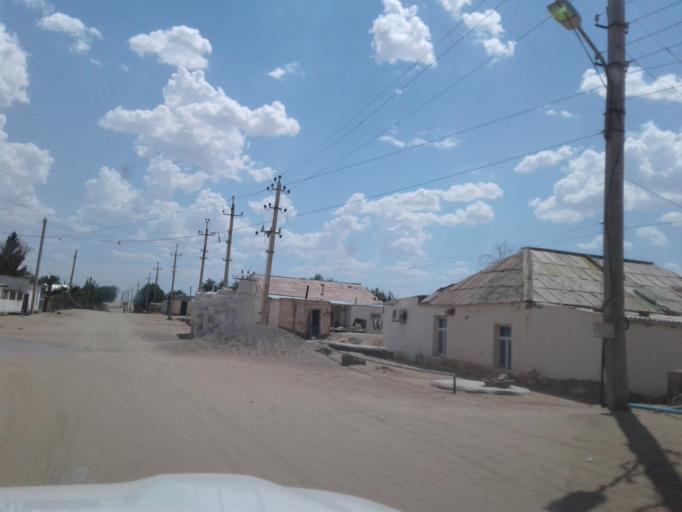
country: TM
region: Ahal
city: Abadan
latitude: 38.7626
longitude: 58.4916
